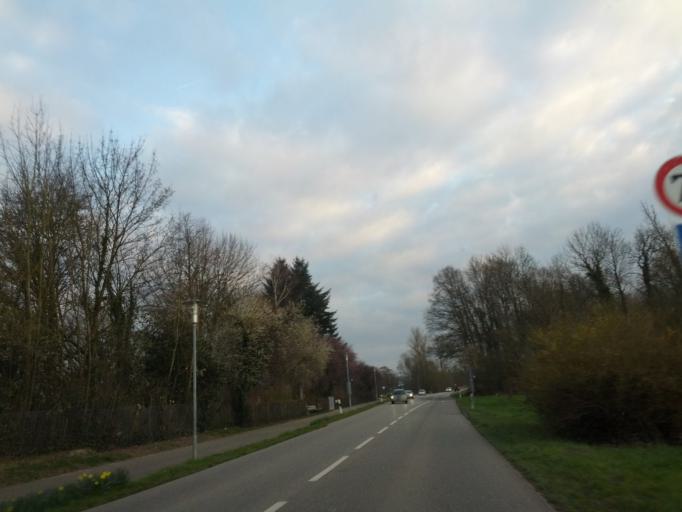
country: DE
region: Baden-Wuerttemberg
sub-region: Freiburg Region
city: Umkirch
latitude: 48.0486
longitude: 7.7802
